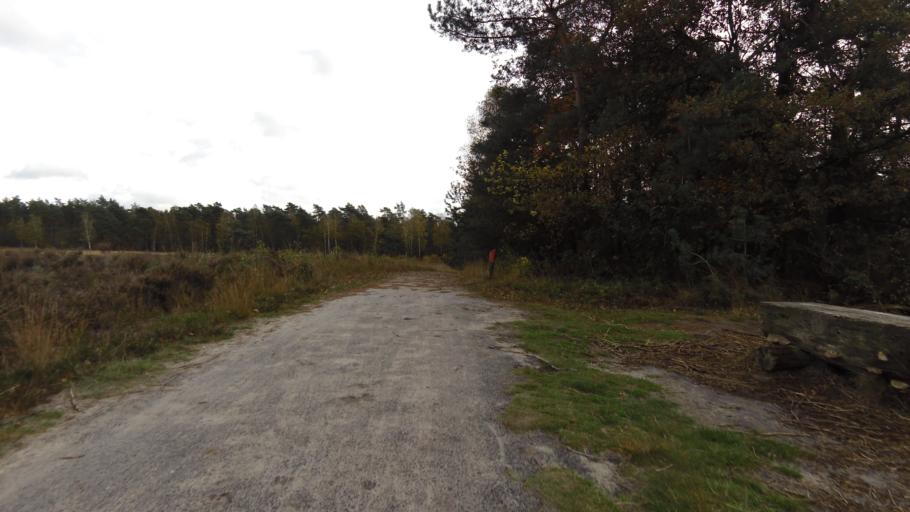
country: NL
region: Gelderland
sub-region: Gemeente Epe
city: Emst
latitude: 52.3304
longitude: 5.9069
